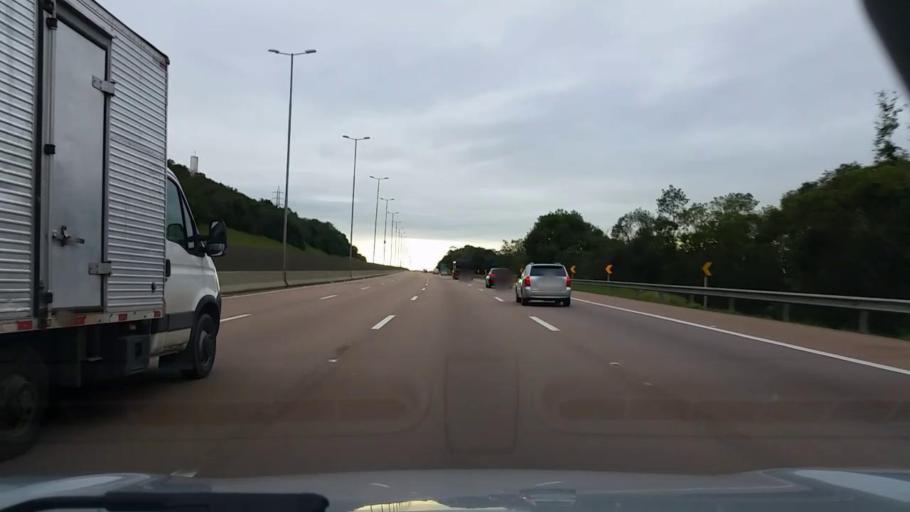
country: BR
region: Rio Grande do Sul
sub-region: Gravatai
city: Gravatai
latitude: -29.9566
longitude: -51.0128
